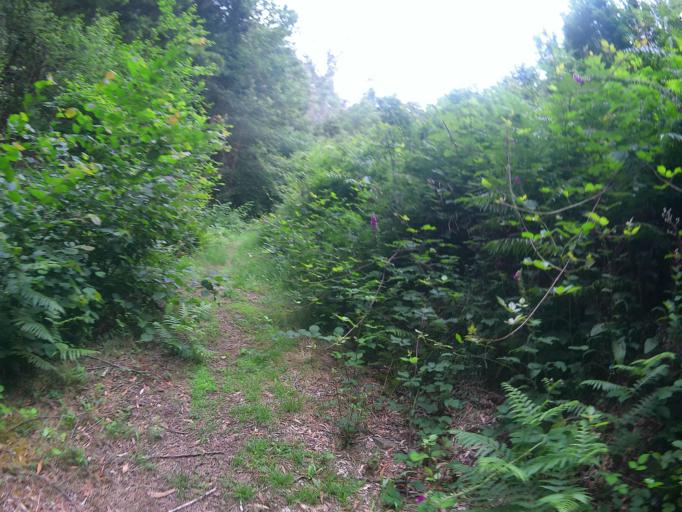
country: PT
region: Aveiro
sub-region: Albergaria-A-Velha
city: Branca
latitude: 40.7682
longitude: -8.4405
